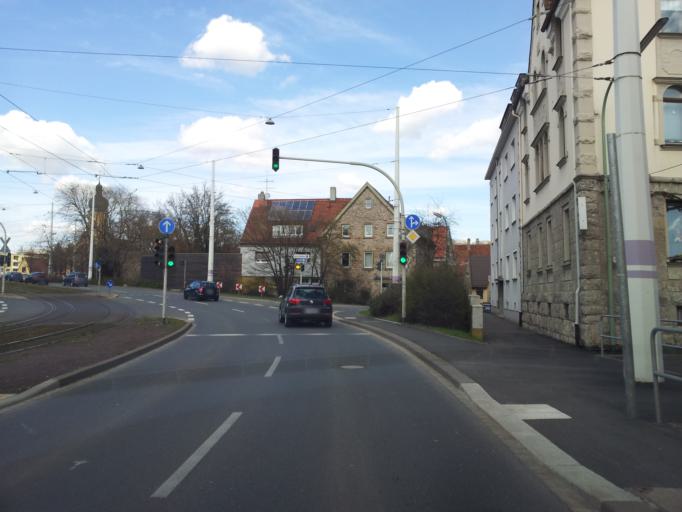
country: DE
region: Bavaria
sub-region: Regierungsbezirk Unterfranken
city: Wuerzburg
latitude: 49.7625
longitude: 9.9447
